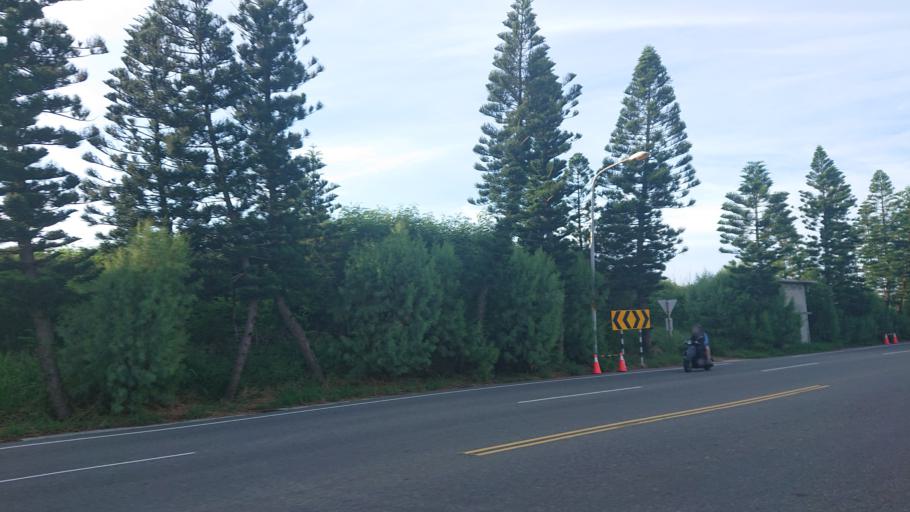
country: TW
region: Taiwan
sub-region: Penghu
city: Ma-kung
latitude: 23.6602
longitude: 119.5571
